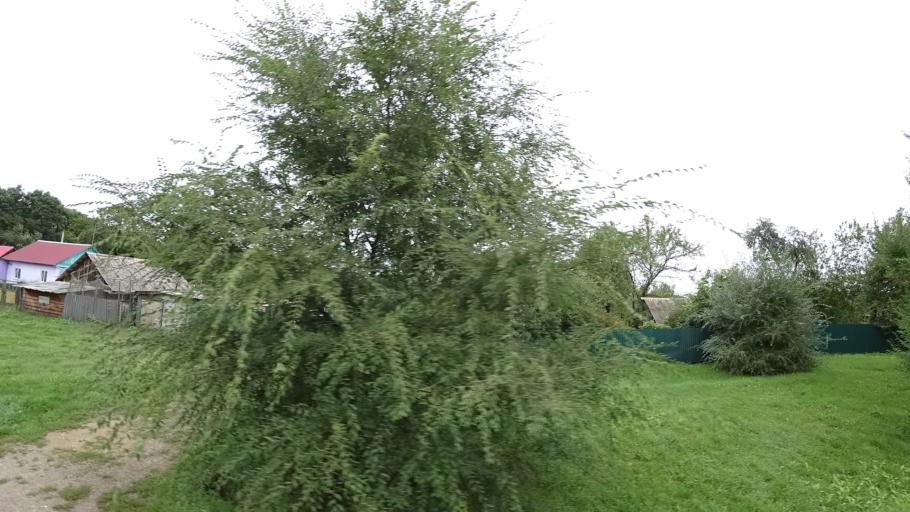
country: RU
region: Primorskiy
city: Monastyrishche
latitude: 44.0883
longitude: 132.5751
